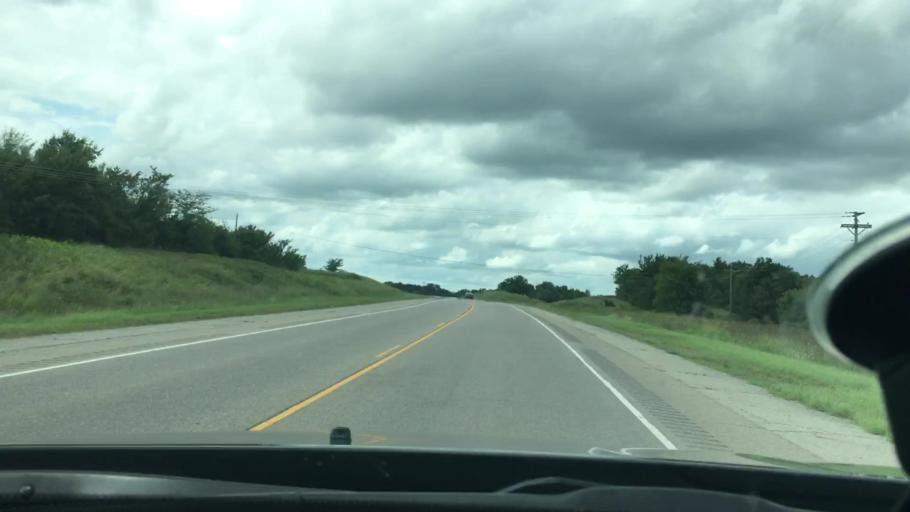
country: US
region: Oklahoma
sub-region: Pontotoc County
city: Ada
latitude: 34.6418
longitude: -96.4916
